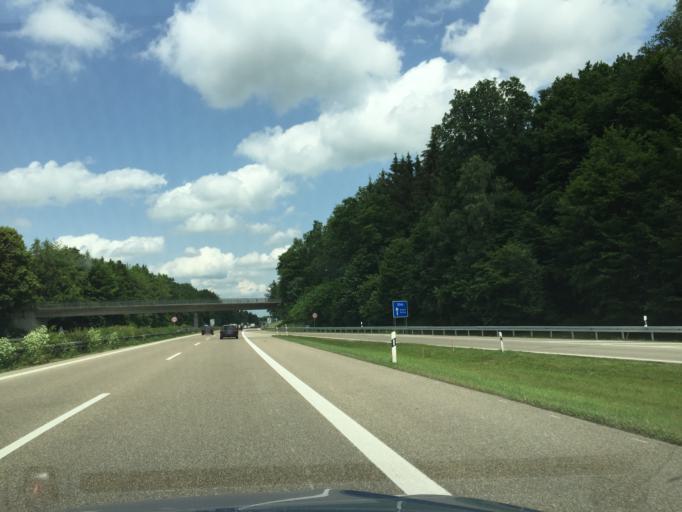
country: DE
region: Bavaria
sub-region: Swabia
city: Holzheim
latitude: 48.3618
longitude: 10.0817
